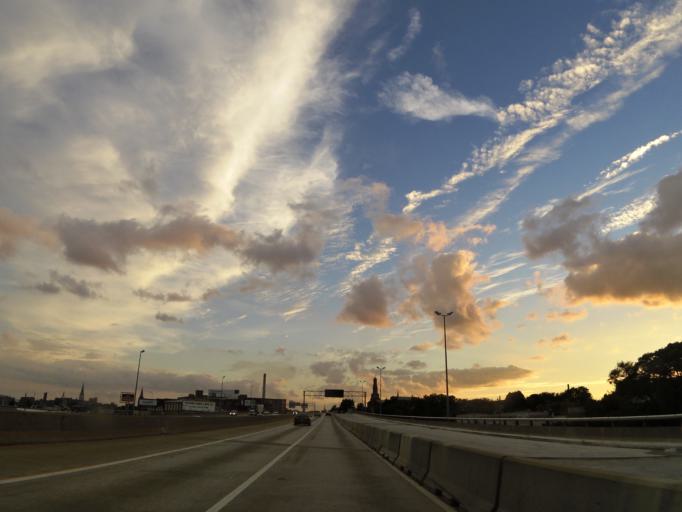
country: US
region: Missouri
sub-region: City of Saint Louis
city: St. Louis
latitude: 38.6144
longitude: -90.1952
